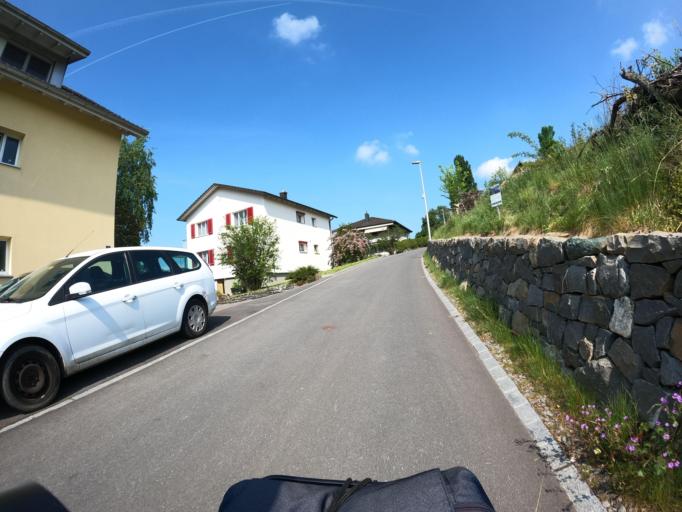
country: CH
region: Zug
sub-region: Zug
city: Steinhausen
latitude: 47.1939
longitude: 8.4957
